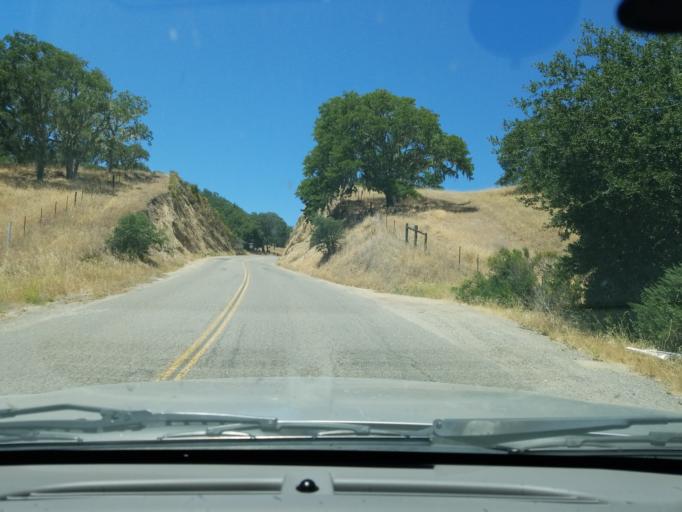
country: US
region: California
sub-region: Monterey County
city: Gonzales
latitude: 36.4017
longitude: -121.5811
